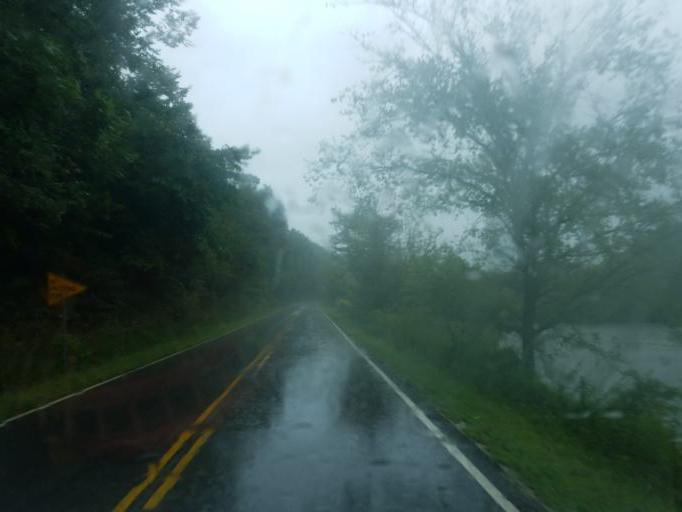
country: US
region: Kentucky
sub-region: Carter County
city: Grayson
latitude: 38.4927
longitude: -83.0197
